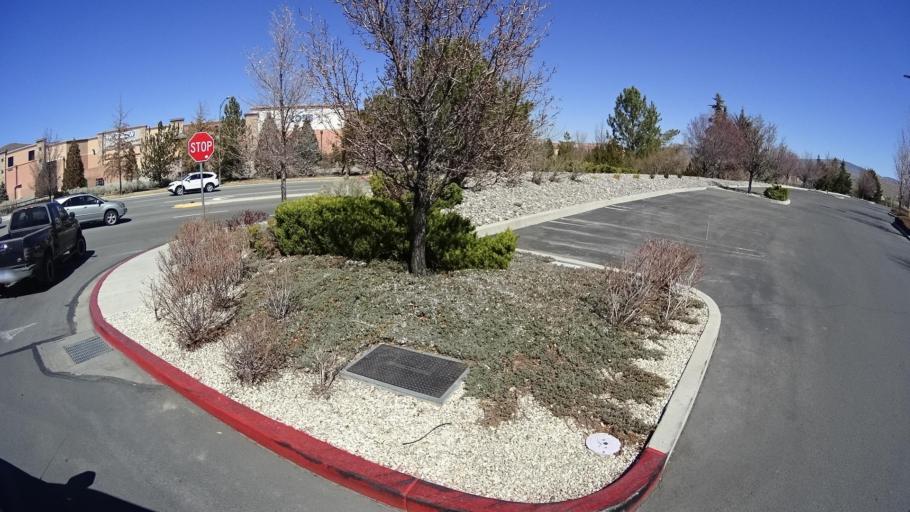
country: US
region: Nevada
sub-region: Washoe County
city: Sun Valley
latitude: 39.5803
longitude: -119.7396
